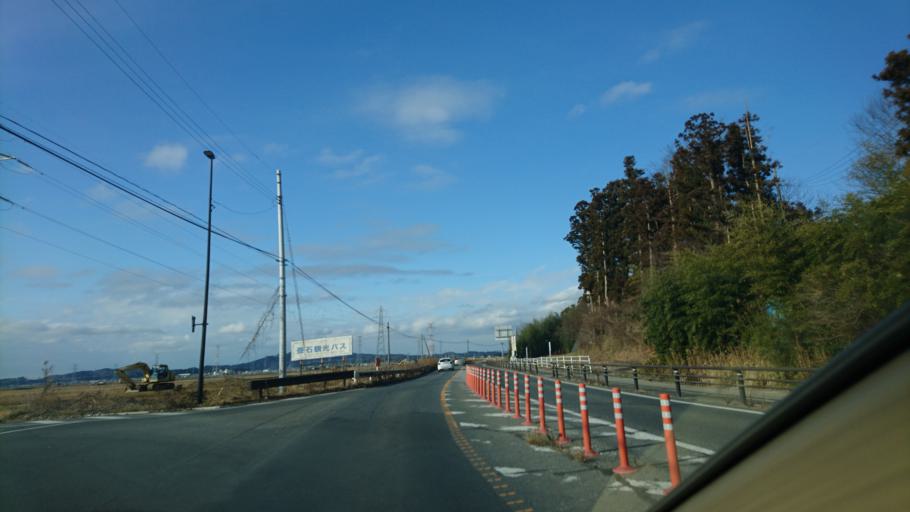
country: JP
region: Miyagi
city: Yamoto
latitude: 38.4605
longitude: 141.2434
